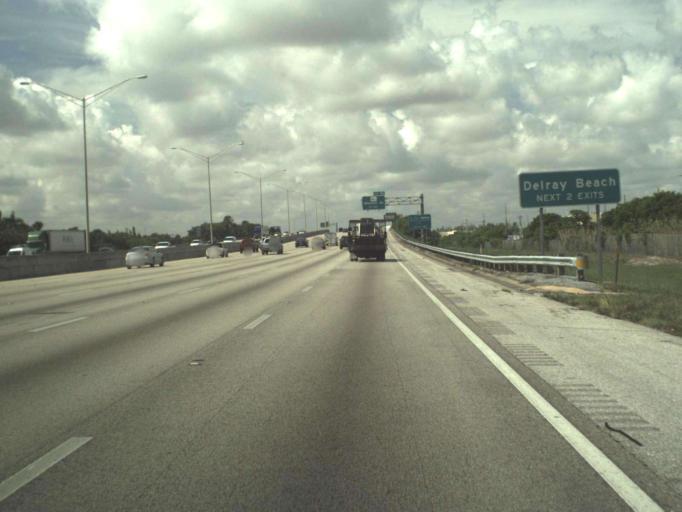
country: US
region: Florida
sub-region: Palm Beach County
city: Delray Beach
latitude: 26.4759
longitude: -80.0877
